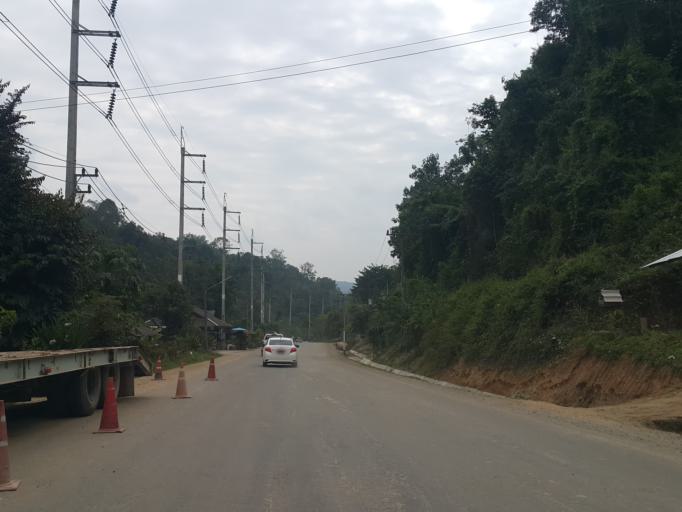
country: TH
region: Chiang Mai
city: Mae Taeng
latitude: 19.1704
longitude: 98.6912
